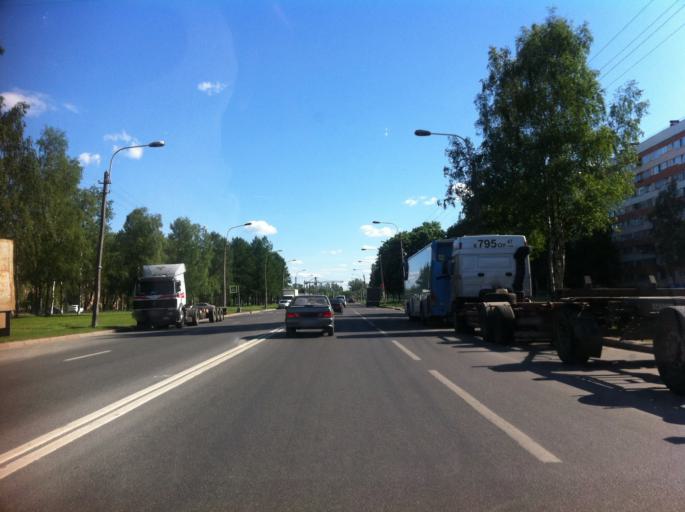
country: RU
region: St.-Petersburg
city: Uritsk
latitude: 59.8280
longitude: 30.1757
